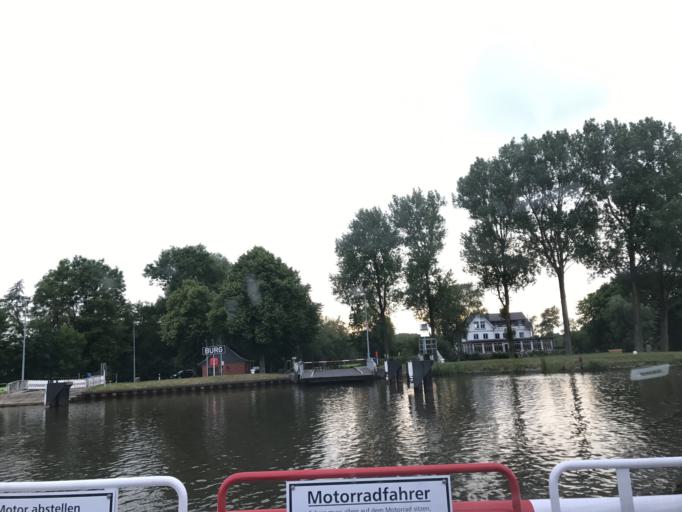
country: DE
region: Schleswig-Holstein
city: Aebtissinwisch
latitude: 53.9833
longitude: 9.2789
